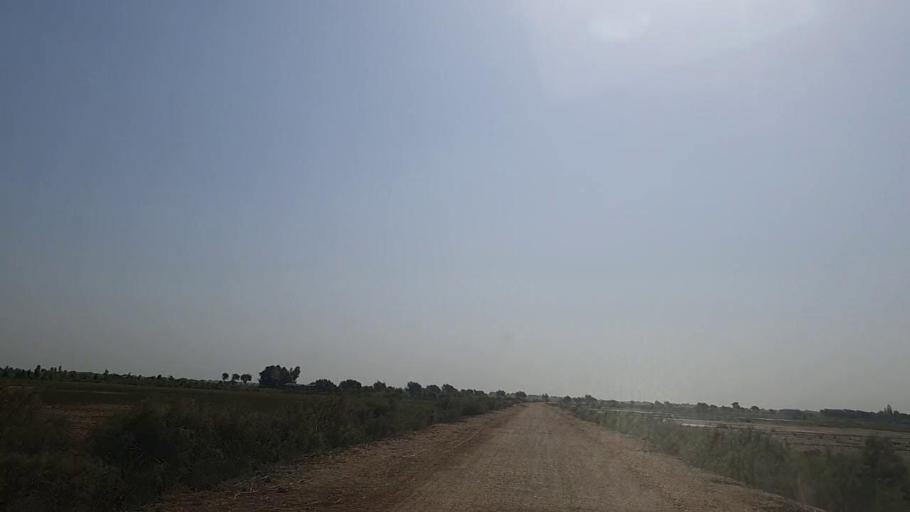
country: PK
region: Sindh
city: Daro Mehar
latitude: 24.7096
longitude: 68.1239
